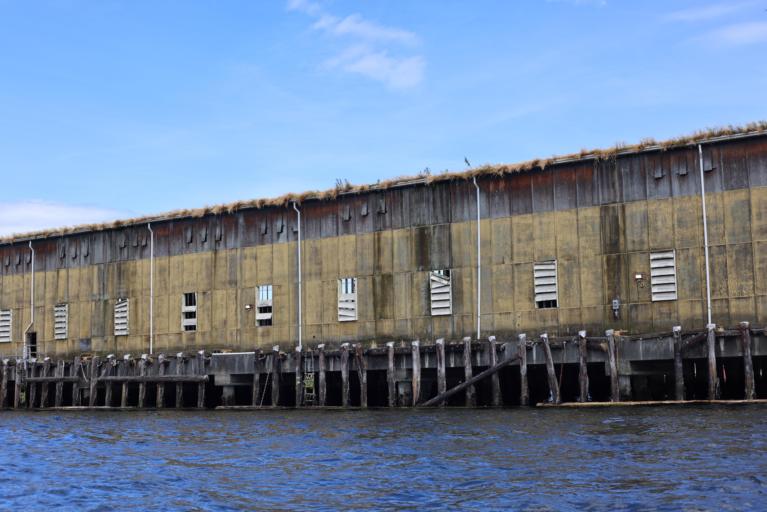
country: CA
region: British Columbia
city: North Cowichan
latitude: 48.8728
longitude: -123.6424
